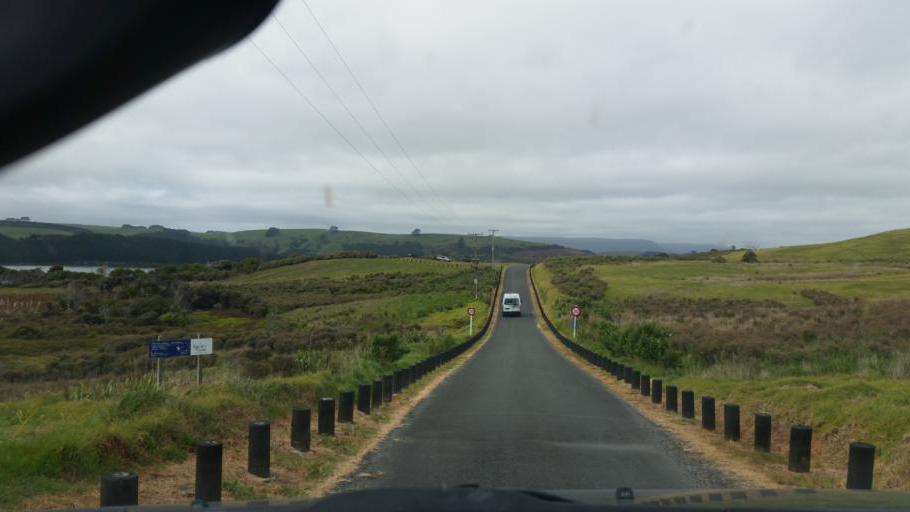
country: NZ
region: Northland
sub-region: Kaipara District
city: Dargaville
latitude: -35.8141
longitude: 173.6420
